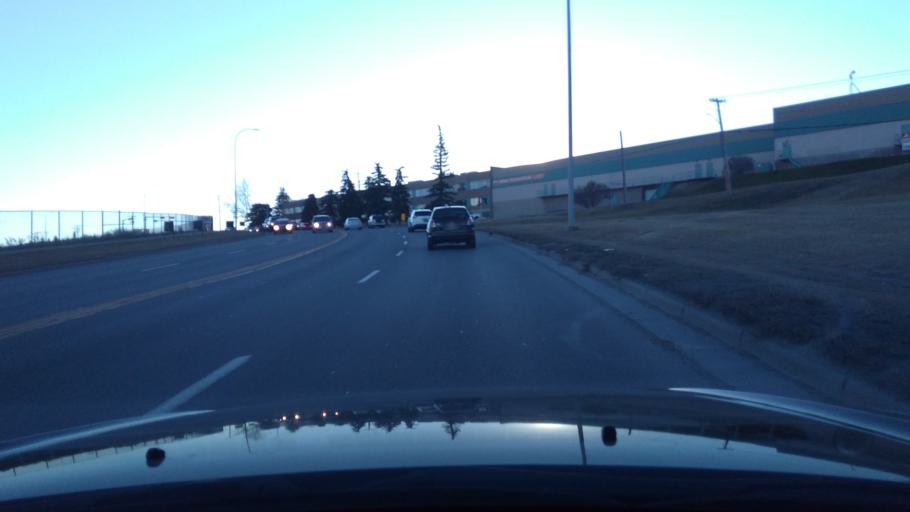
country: CA
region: Alberta
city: Calgary
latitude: 50.9865
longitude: -114.0473
